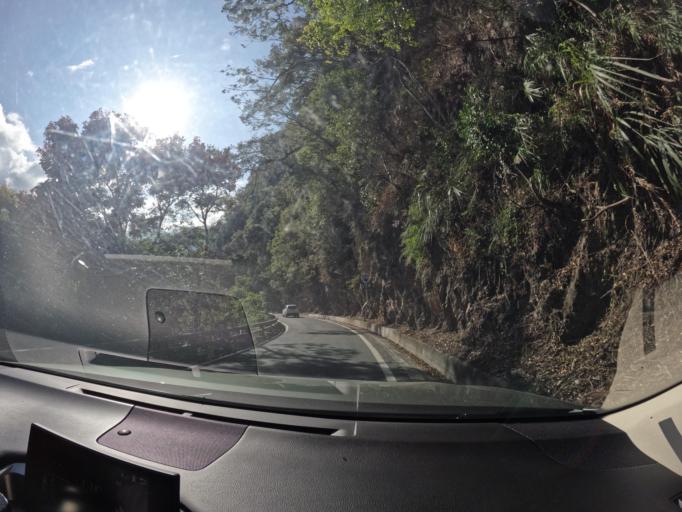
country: TW
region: Taiwan
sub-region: Taitung
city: Taitung
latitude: 23.1776
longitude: 121.0423
